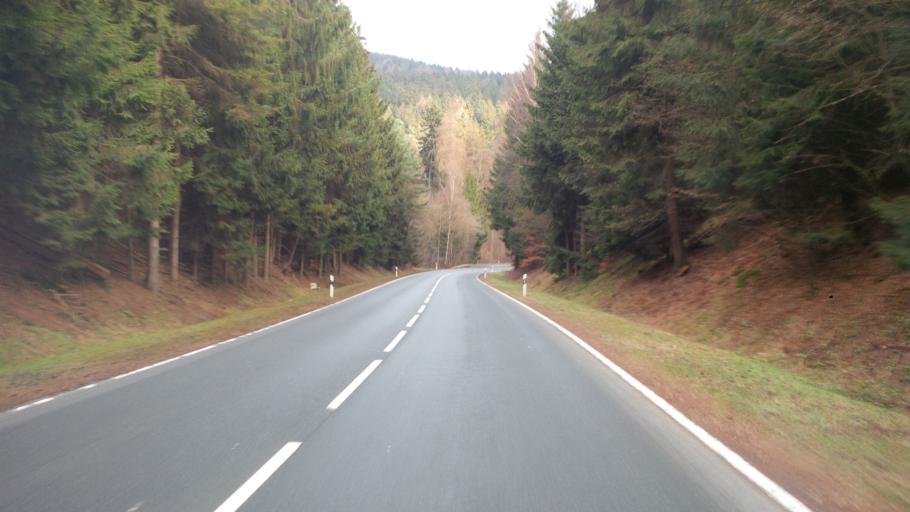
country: DE
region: Hesse
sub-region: Regierungsbezirk Darmstadt
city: Schmitten
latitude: 50.2315
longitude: 8.4930
